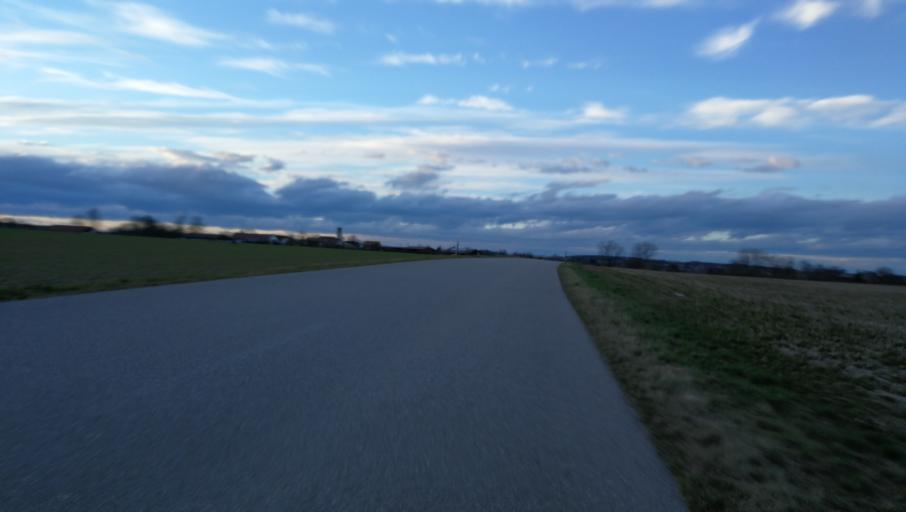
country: DE
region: Bavaria
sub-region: Upper Bavaria
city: Fuerstenfeldbruck
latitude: 48.2055
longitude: 11.2274
